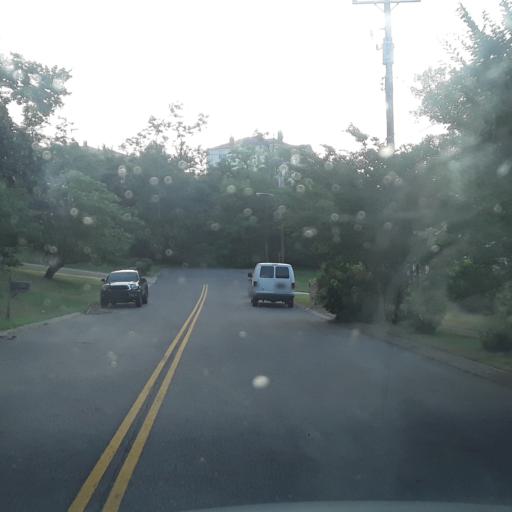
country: US
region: Tennessee
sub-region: Williamson County
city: Brentwood Estates
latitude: 36.0468
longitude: -86.7235
